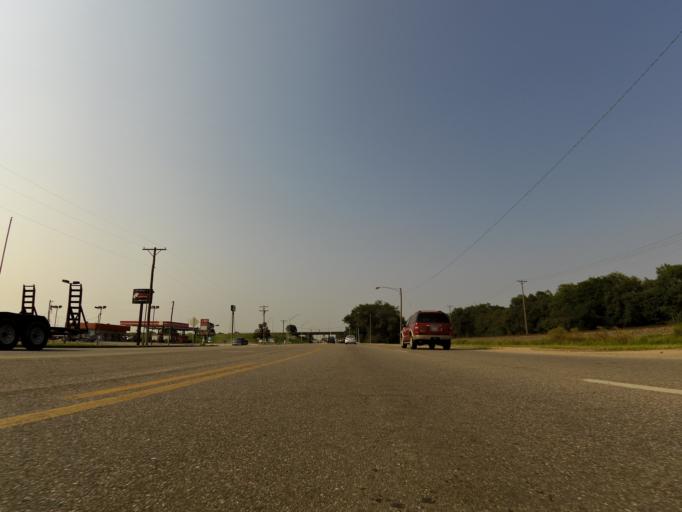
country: US
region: Kansas
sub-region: Sedgwick County
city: Park City
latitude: 37.7546
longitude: -97.3360
